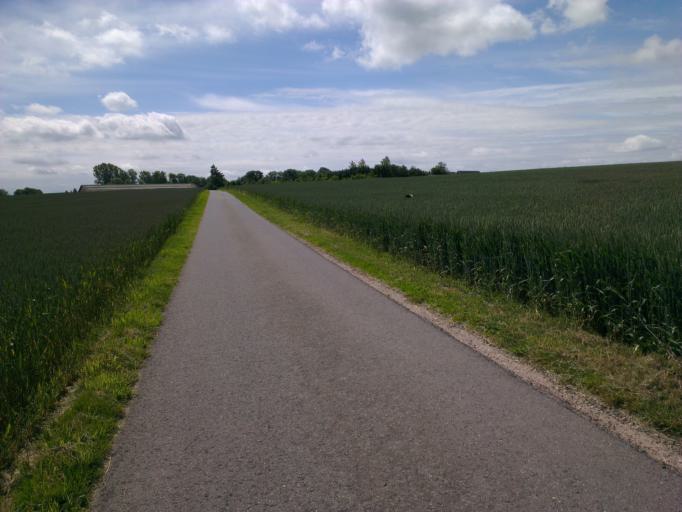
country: DK
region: Capital Region
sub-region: Frederikssund Kommune
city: Skibby
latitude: 55.7910
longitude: 11.9900
